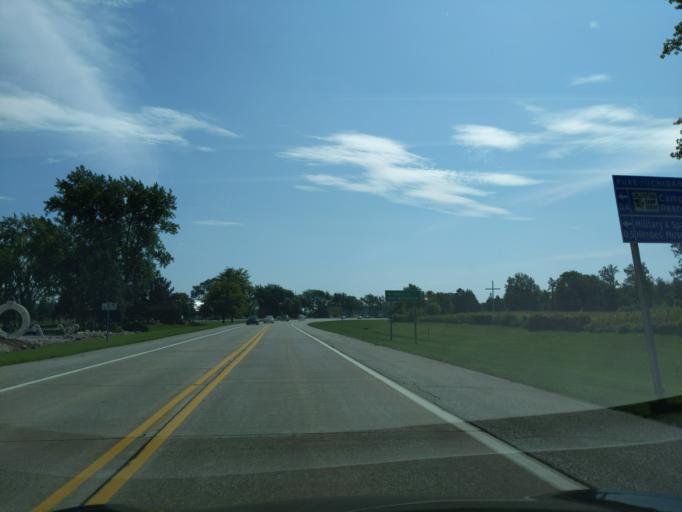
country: US
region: Michigan
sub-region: Saginaw County
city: Frankenmuth
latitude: 43.3126
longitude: -83.7373
